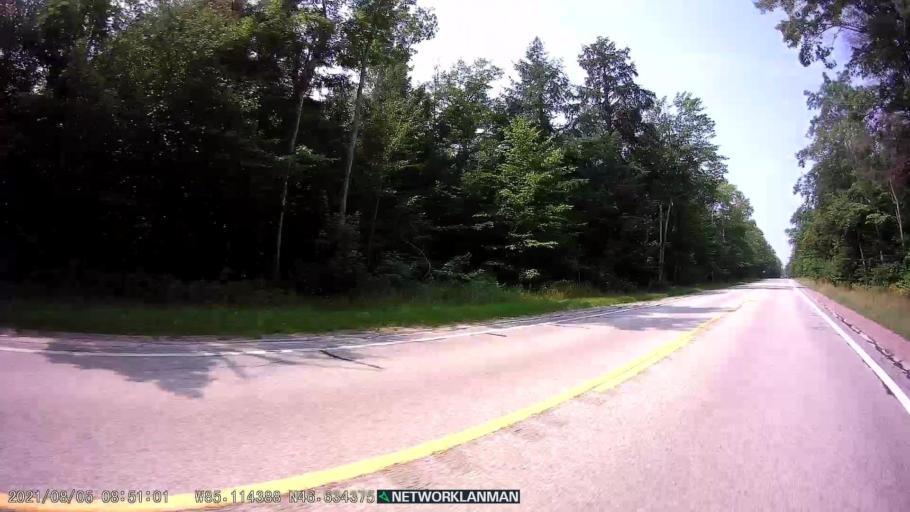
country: US
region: Michigan
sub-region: Luce County
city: Newberry
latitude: 46.6342
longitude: -85.1157
